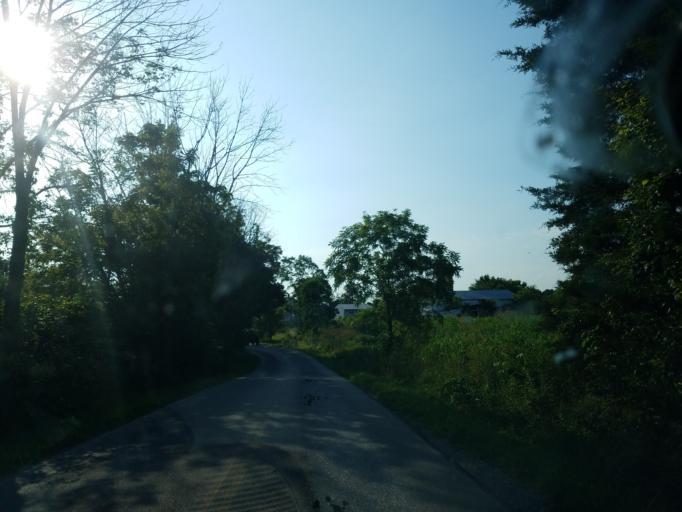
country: US
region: Ohio
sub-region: Adams County
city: West Union
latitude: 38.8825
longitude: -83.4960
